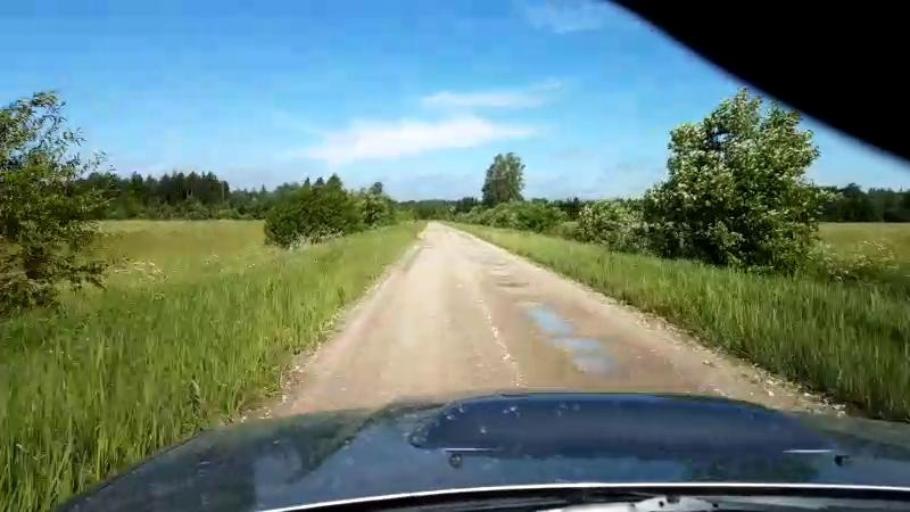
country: EE
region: Paernumaa
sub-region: Sindi linn
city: Sindi
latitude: 58.5076
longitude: 24.6930
